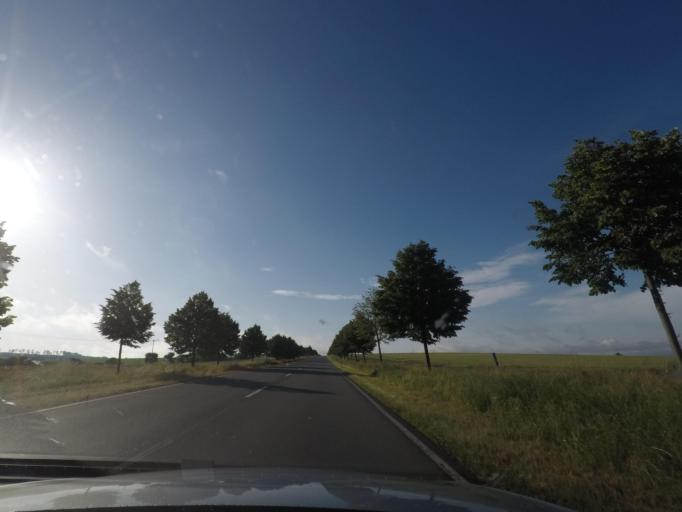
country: DE
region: Saxony-Anhalt
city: Huy-Neinstedt
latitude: 51.9688
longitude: 10.8537
